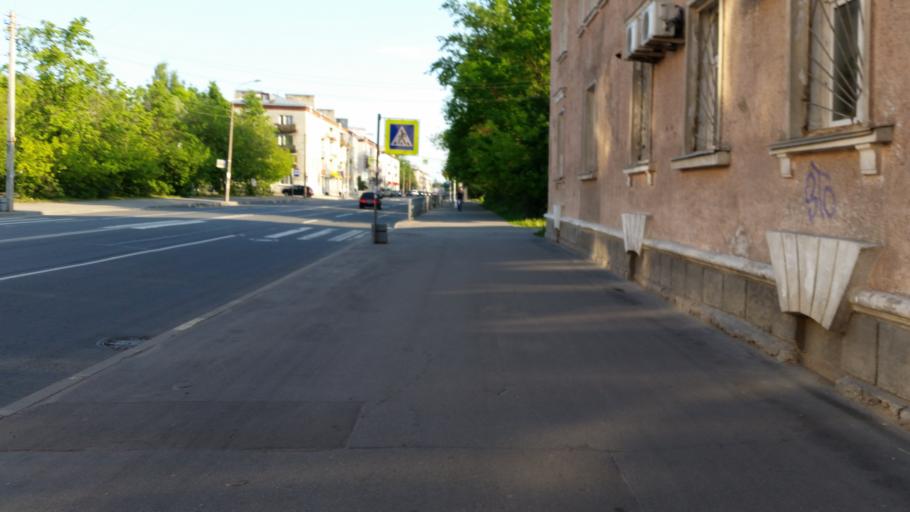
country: RU
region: St.-Petersburg
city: Sosnovaya Polyana
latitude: 59.8419
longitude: 30.1467
